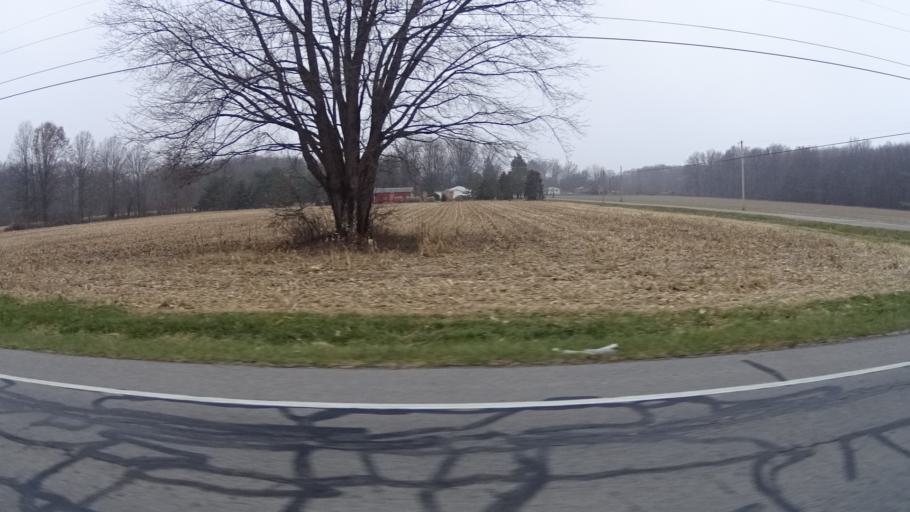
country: US
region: Ohio
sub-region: Lorain County
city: South Amherst
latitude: 41.3138
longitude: -82.2726
